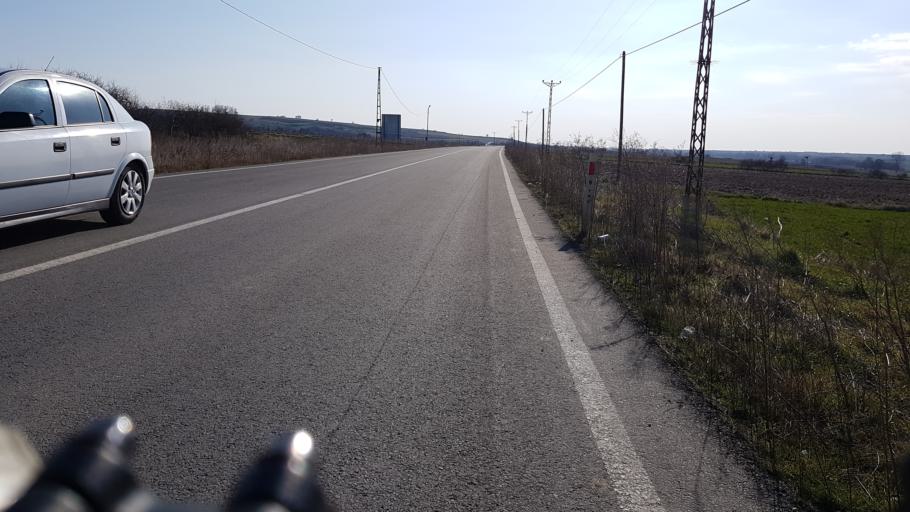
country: TR
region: Tekirdag
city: Saray
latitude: 41.3682
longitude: 27.8611
